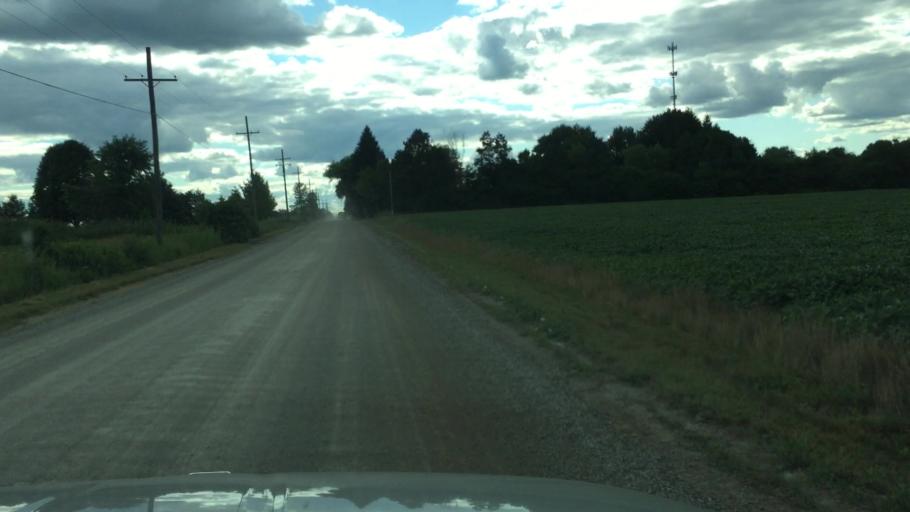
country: US
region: Michigan
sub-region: Saint Clair County
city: Yale
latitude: 43.1443
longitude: -82.8049
